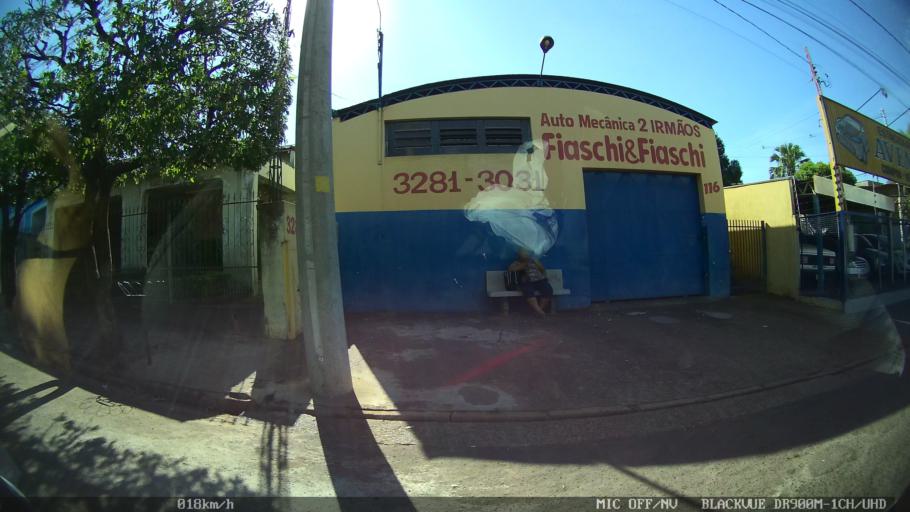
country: BR
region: Sao Paulo
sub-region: Olimpia
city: Olimpia
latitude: -20.7394
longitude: -48.9045
